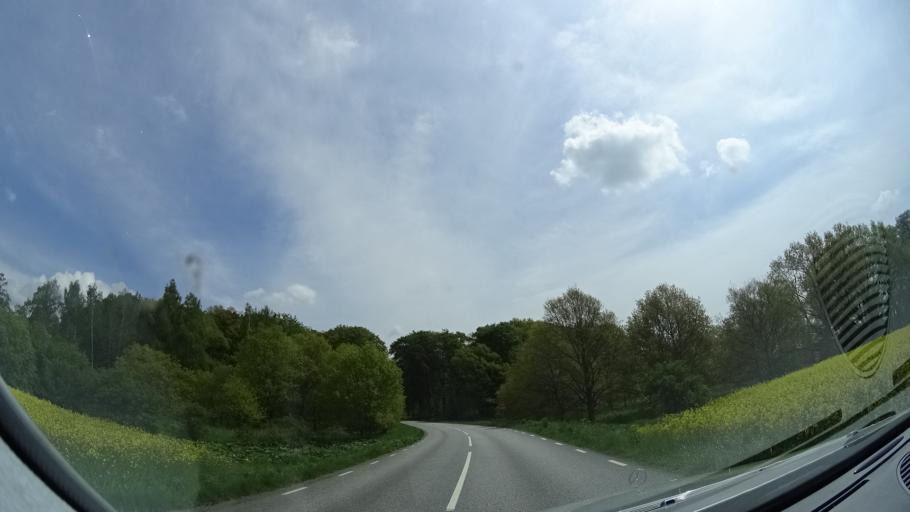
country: SE
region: Skane
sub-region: Sjobo Kommun
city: Blentarp
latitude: 55.6919
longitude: 13.6125
